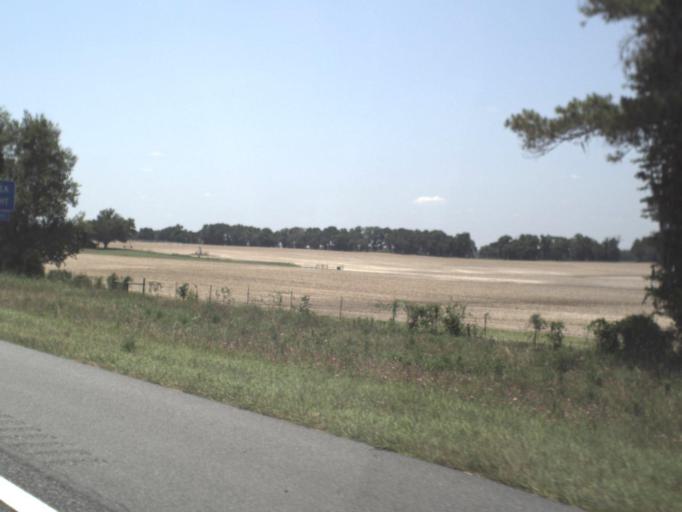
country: US
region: Florida
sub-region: Suwannee County
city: Wellborn
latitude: 30.2717
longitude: -82.7766
